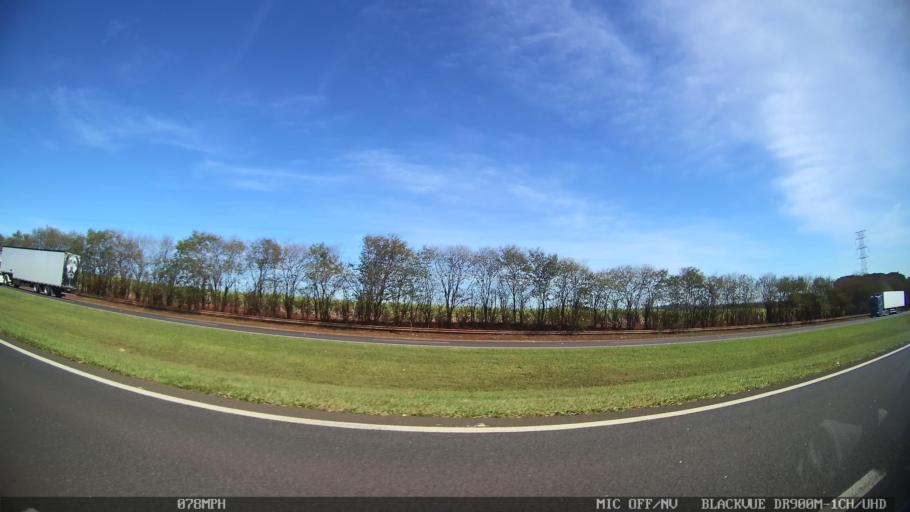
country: BR
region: Sao Paulo
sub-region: Araras
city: Araras
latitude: -22.3187
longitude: -47.3902
